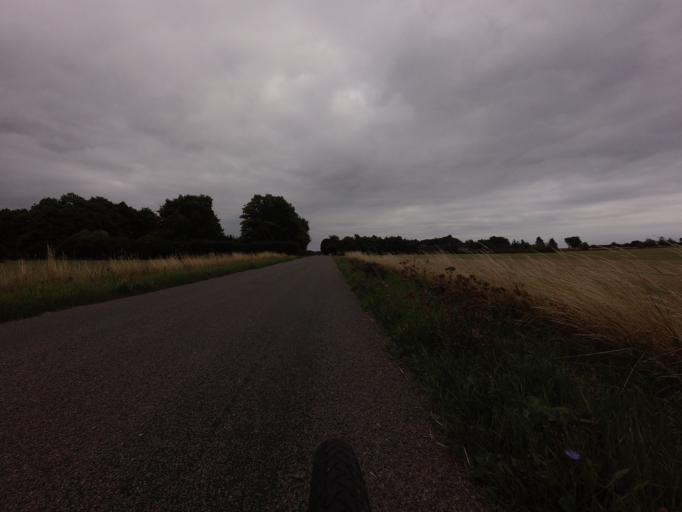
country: DK
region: Zealand
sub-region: Stevns Kommune
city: Store Heddinge
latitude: 55.3285
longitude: 12.4466
